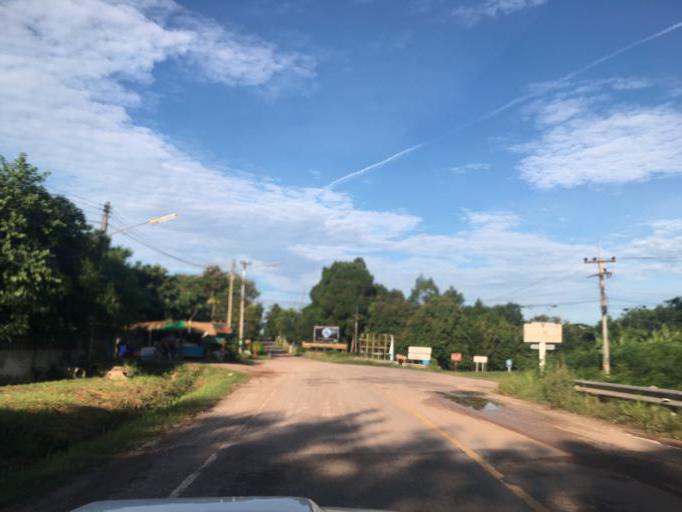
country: TH
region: Changwat Udon Thani
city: Kut Chap
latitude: 17.3803
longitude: 102.6056
